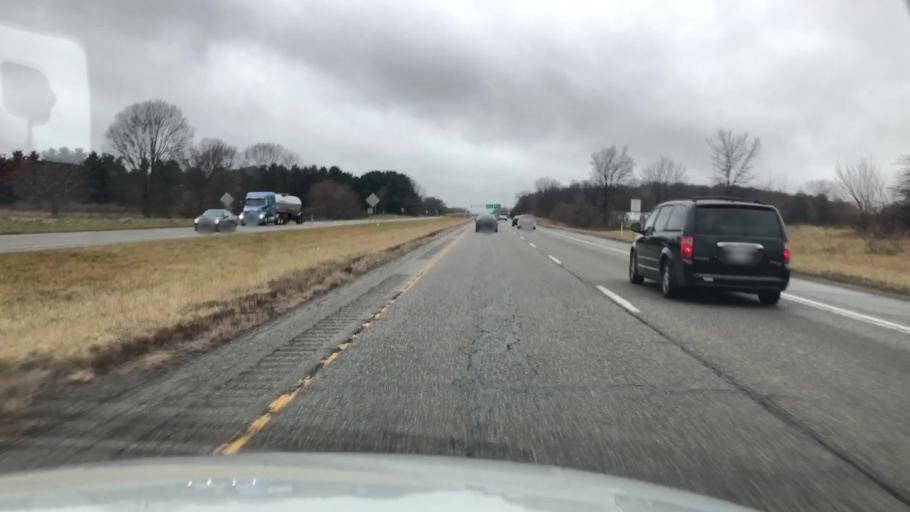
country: US
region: Indiana
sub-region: Marshall County
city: Plymouth
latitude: 41.3437
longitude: -86.2642
